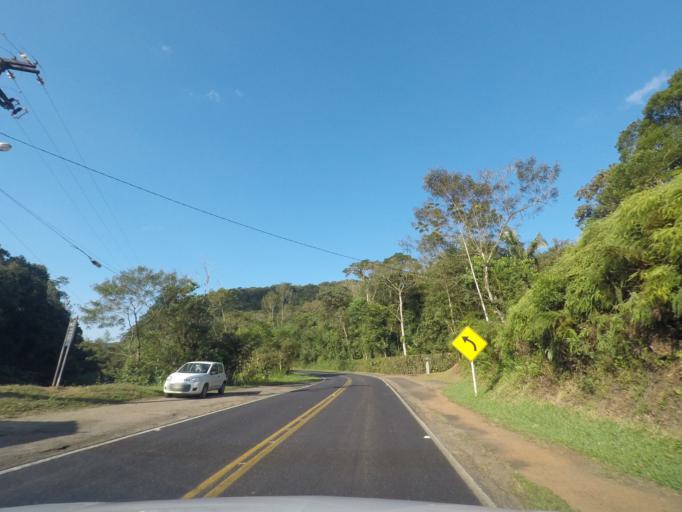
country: BR
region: Parana
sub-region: Antonina
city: Antonina
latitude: -25.3969
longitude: -48.8686
